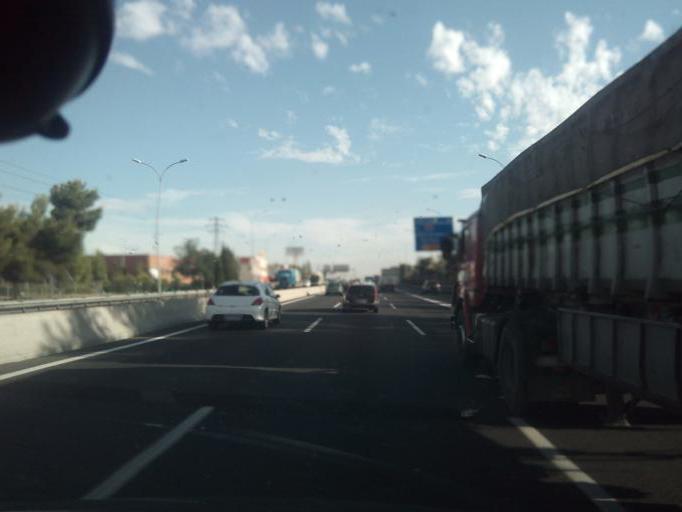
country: ES
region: Madrid
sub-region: Provincia de Madrid
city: Pinto
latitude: 40.2447
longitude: -3.6899
